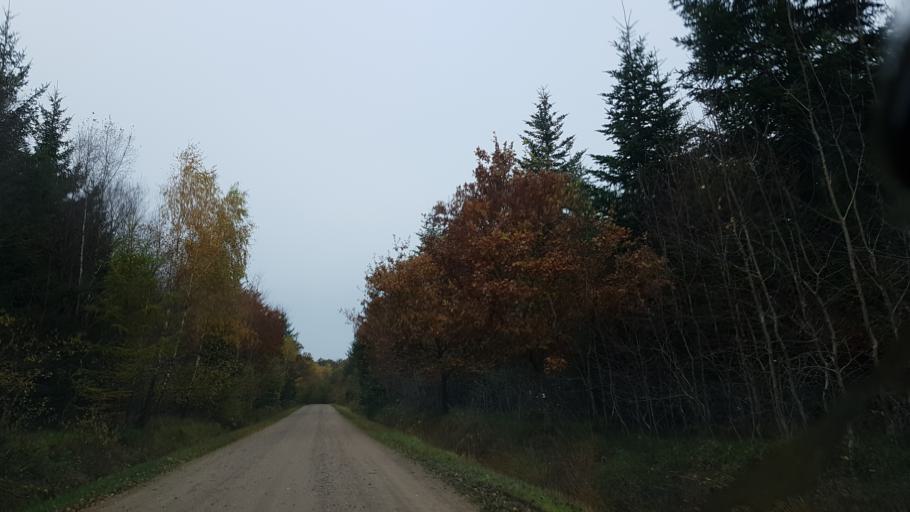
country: DK
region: South Denmark
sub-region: Tonder Kommune
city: Sherrebek
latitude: 55.1891
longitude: 8.7585
